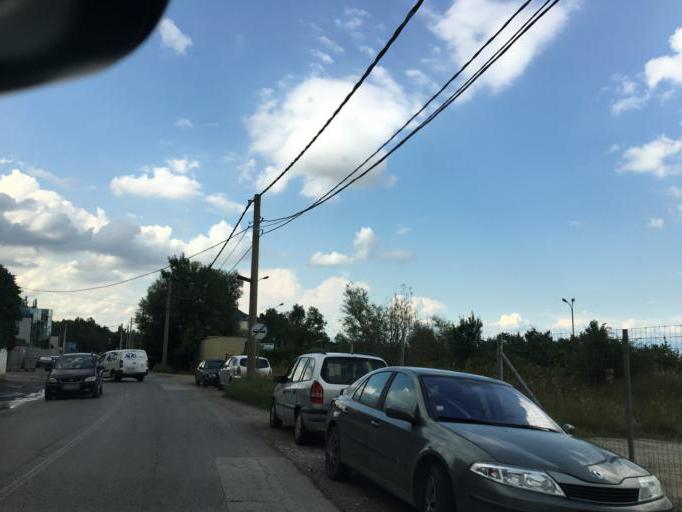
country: BG
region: Sofia-Capital
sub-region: Stolichna Obshtina
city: Sofia
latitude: 42.6284
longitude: 23.3577
